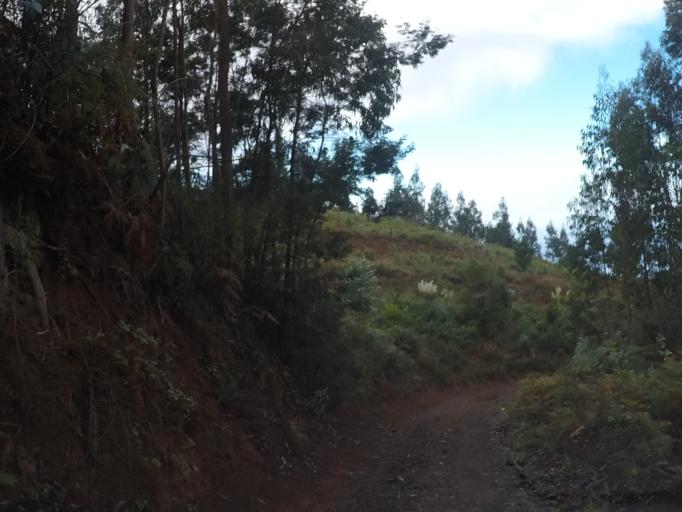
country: PT
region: Madeira
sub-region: Funchal
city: Nossa Senhora do Monte
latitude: 32.6772
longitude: -16.8770
